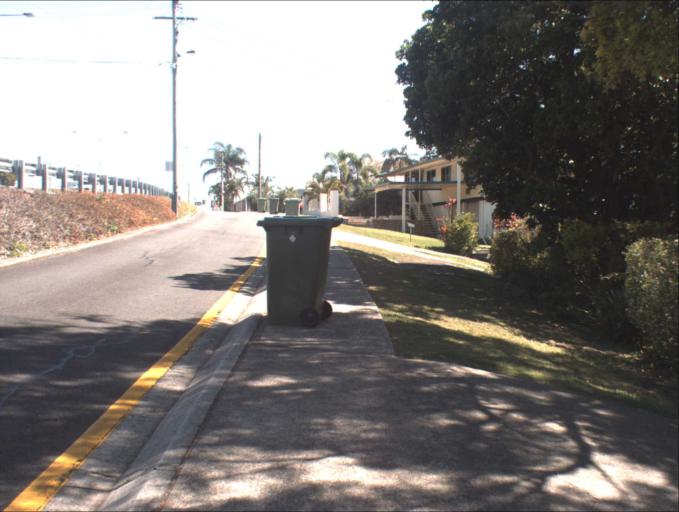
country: AU
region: Queensland
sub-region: Logan
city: Rochedale South
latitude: -27.6000
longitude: 153.1101
